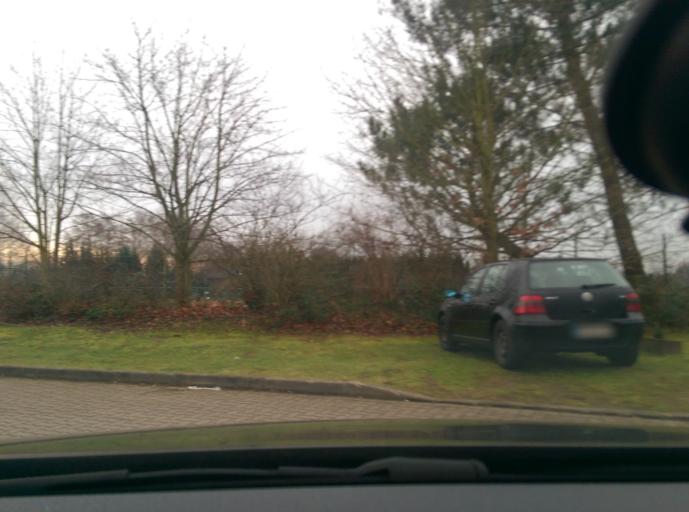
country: DE
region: Lower Saxony
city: Elze
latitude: 52.5456
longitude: 9.7494
